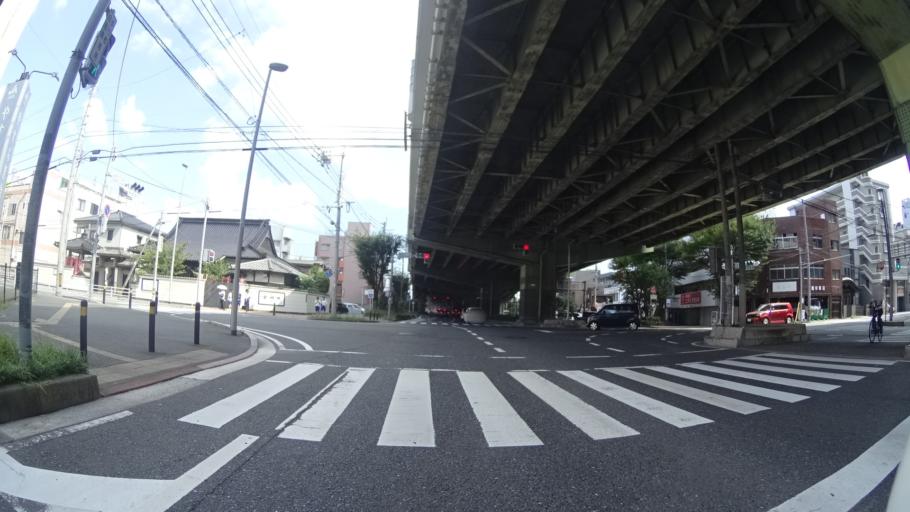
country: JP
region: Fukuoka
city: Kitakyushu
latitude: 33.8468
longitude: 130.8799
